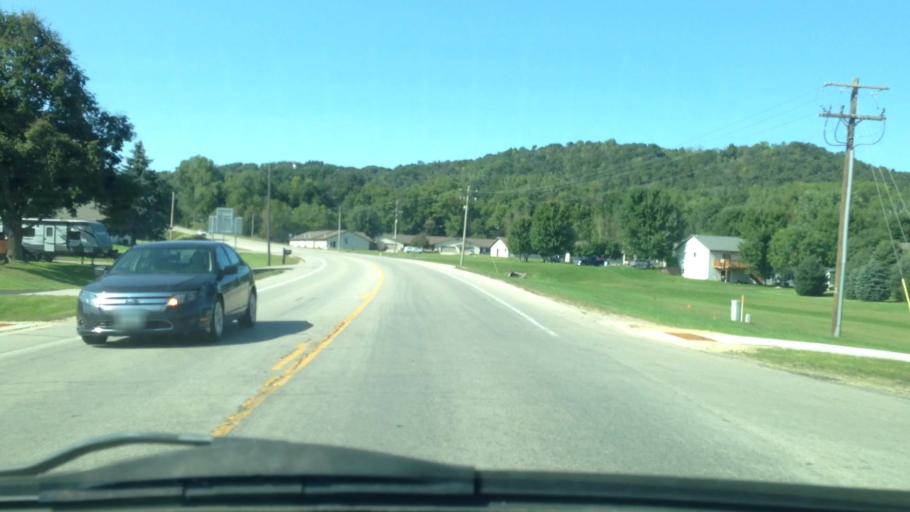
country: US
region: Minnesota
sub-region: Fillmore County
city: Rushford
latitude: 43.8177
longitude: -91.7535
